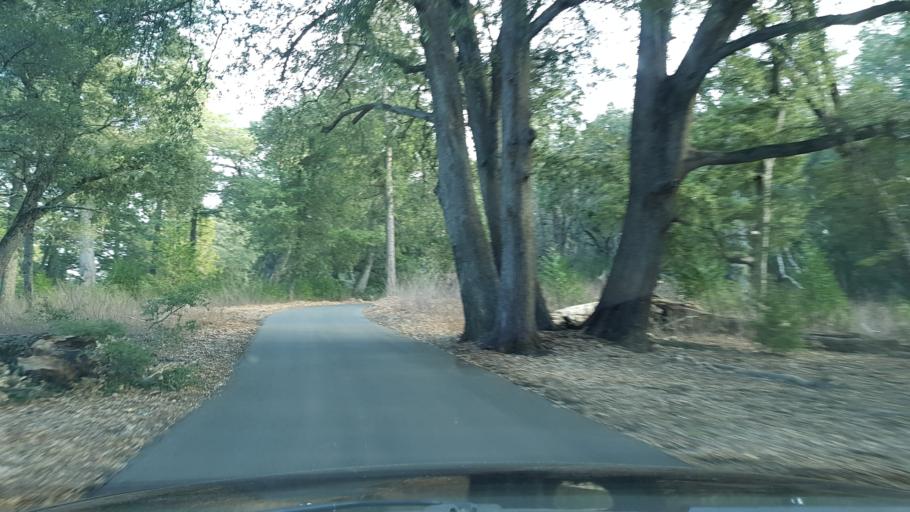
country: US
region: California
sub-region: Riverside County
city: Aguanga
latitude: 33.3418
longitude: -116.9107
